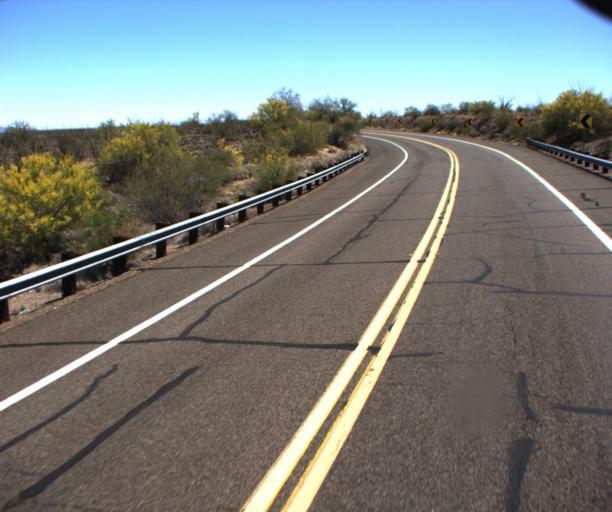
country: US
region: Arizona
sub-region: La Paz County
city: Quartzsite
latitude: 33.6600
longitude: -114.0144
